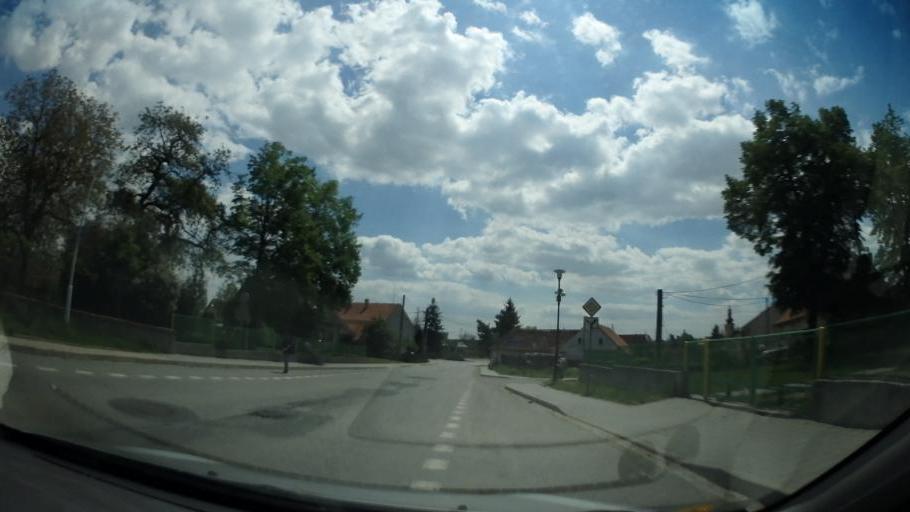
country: CZ
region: Vysocina
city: Hrotovice
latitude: 49.1297
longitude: 16.0817
